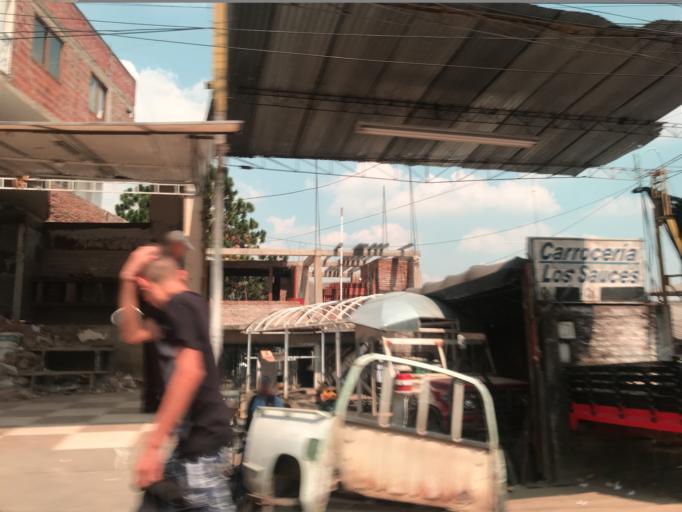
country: CO
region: Valle del Cauca
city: Cali
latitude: 3.4541
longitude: -76.5745
